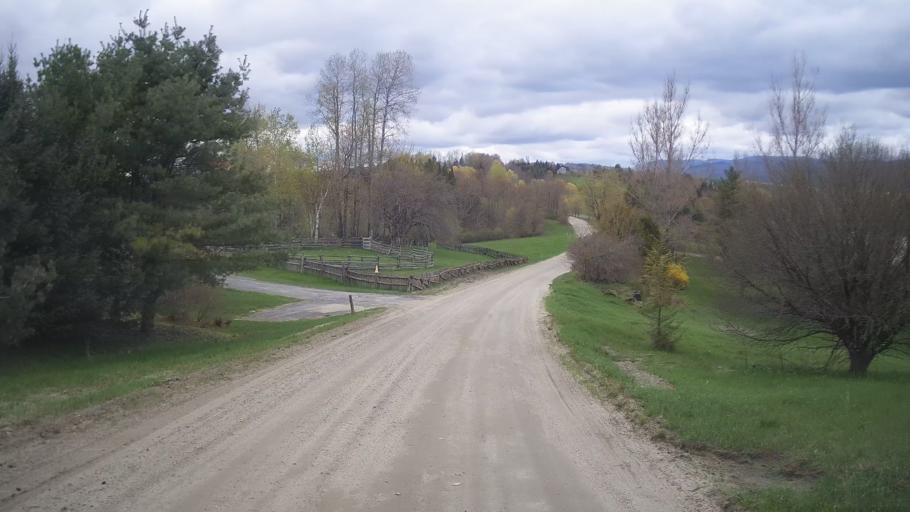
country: US
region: Vermont
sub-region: Caledonia County
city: Lyndonville
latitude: 44.6007
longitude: -71.9533
